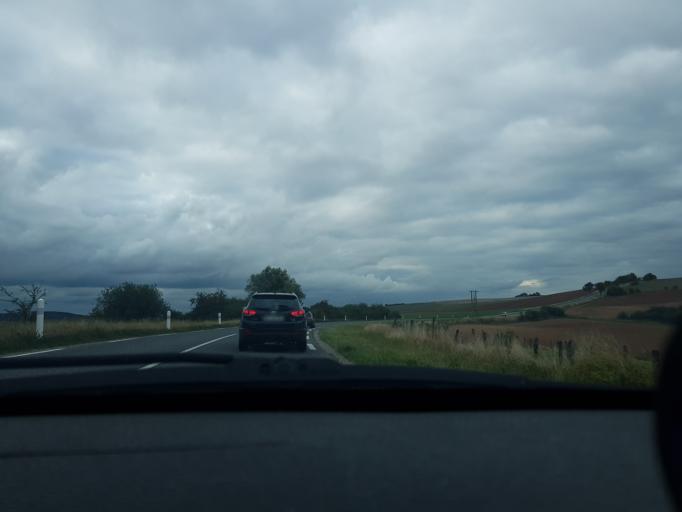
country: FR
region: Lorraine
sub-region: Departement de la Moselle
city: Morhange
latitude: 48.9058
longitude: 6.5593
